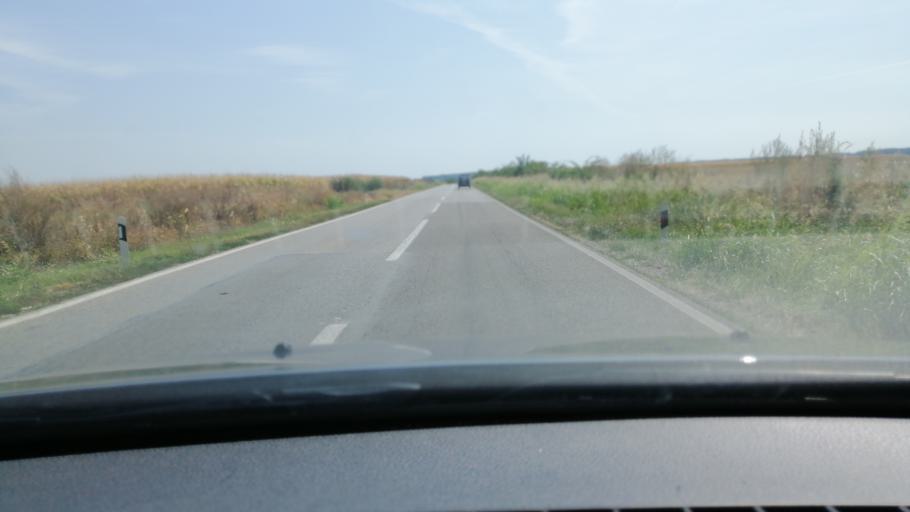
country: RS
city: Sutjeska
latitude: 45.3799
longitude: 20.7286
